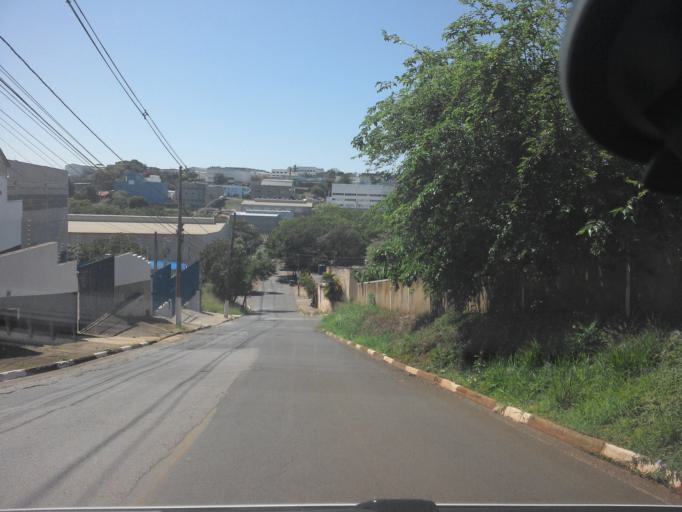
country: BR
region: Sao Paulo
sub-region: Campinas
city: Campinas
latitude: -22.8463
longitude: -47.0477
